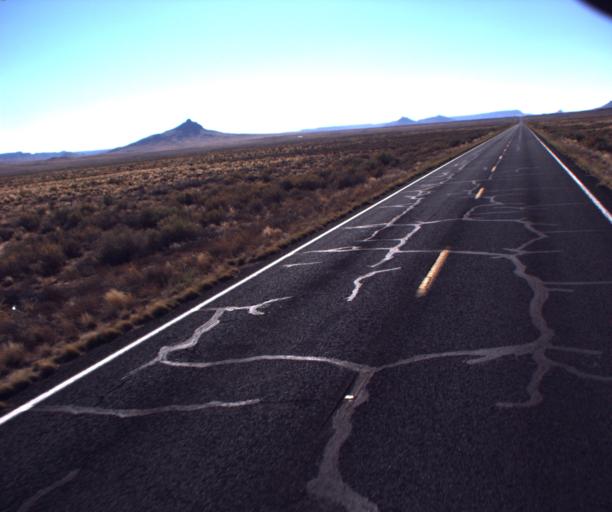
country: US
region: Arizona
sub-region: Navajo County
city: Dilkon
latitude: 35.5835
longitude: -110.4648
